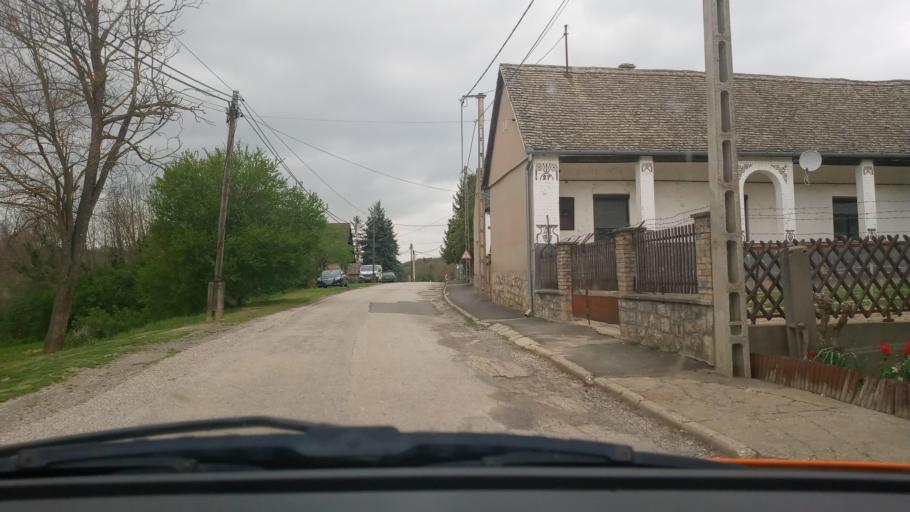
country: HU
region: Baranya
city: Boly
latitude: 46.0074
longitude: 18.5485
